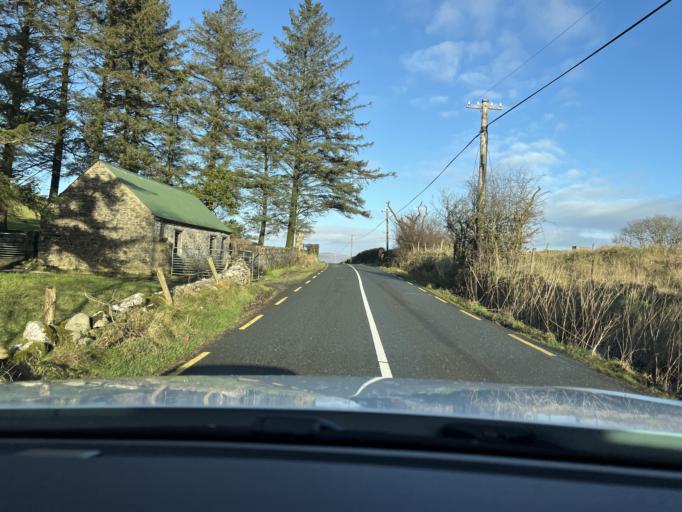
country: IE
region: Connaught
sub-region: County Leitrim
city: Manorhamilton
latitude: 54.2833
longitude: -8.2637
